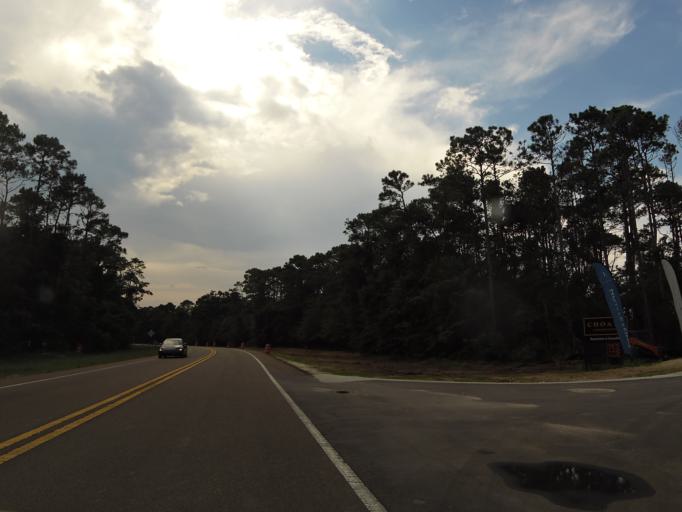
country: US
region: Florida
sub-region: Nassau County
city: Fernandina Beach
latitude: 30.6209
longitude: -81.4622
